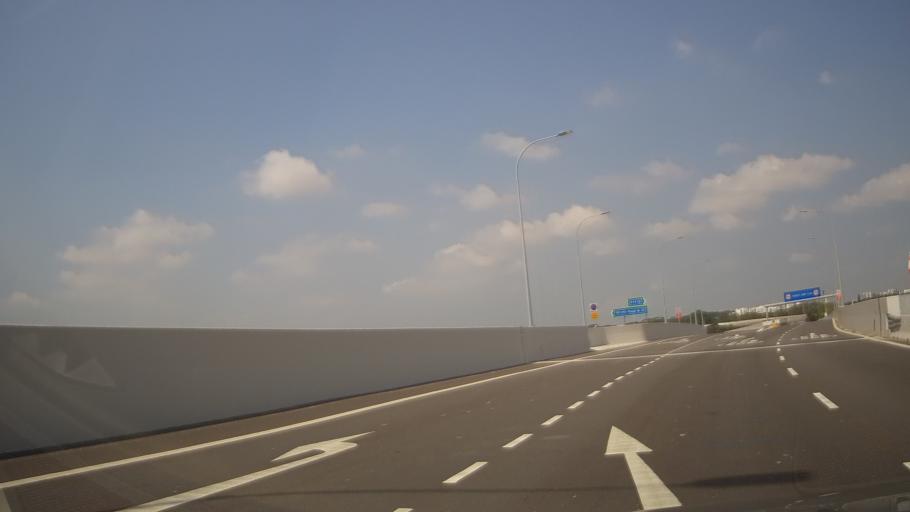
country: MY
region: Johor
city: Kampung Pasir Gudang Baru
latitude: 1.3852
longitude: 103.9207
